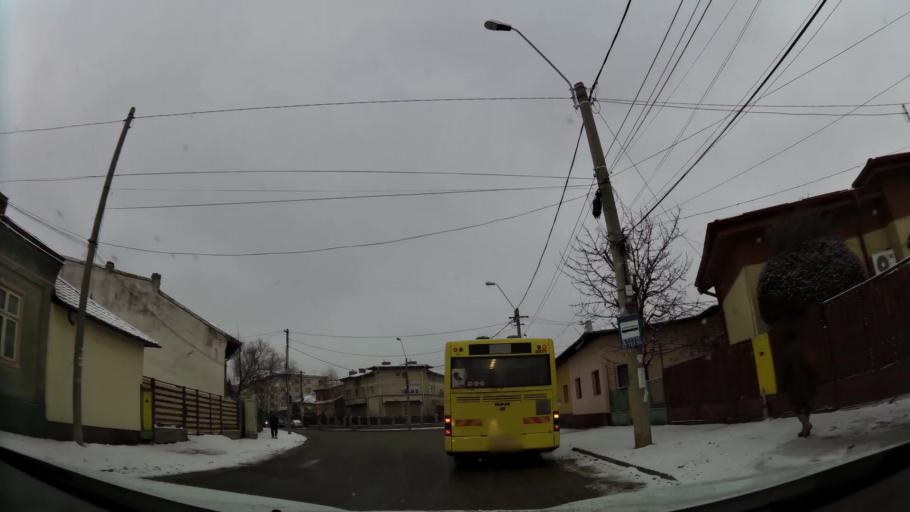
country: RO
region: Prahova
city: Ploiesti
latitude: 44.9338
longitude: 26.0354
